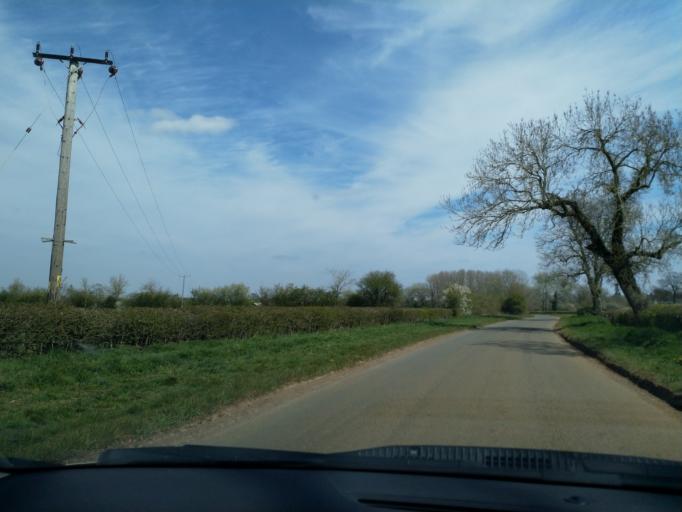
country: GB
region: England
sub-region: Oxfordshire
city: Adderbury
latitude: 52.0739
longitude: -1.2576
